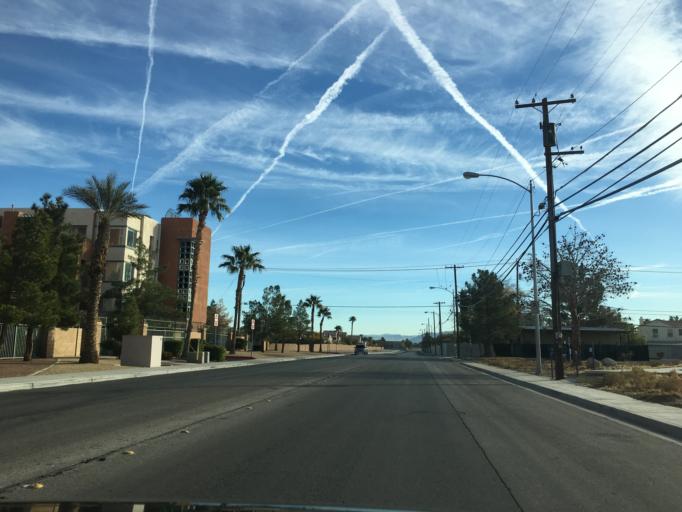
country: US
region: Nevada
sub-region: Clark County
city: Enterprise
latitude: 36.0209
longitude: -115.1690
